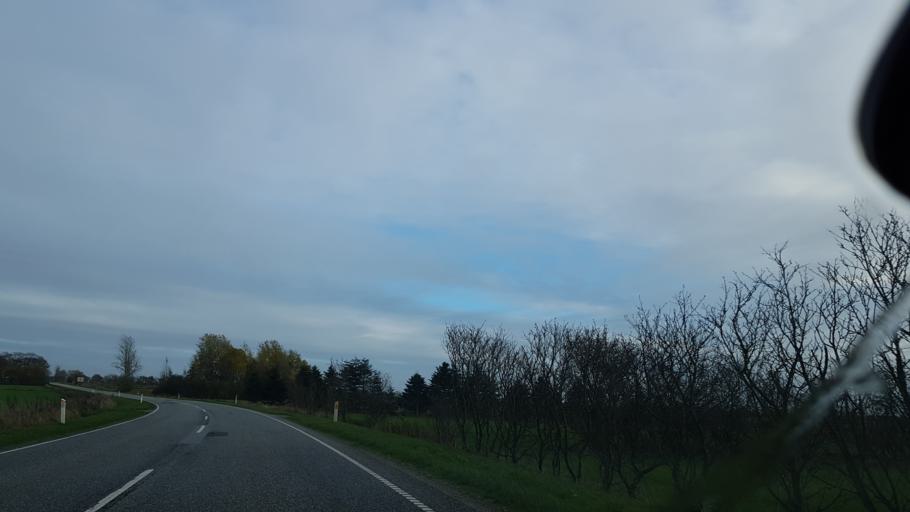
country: DK
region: South Denmark
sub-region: Haderslev Kommune
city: Gram
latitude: 55.2315
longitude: 8.9504
